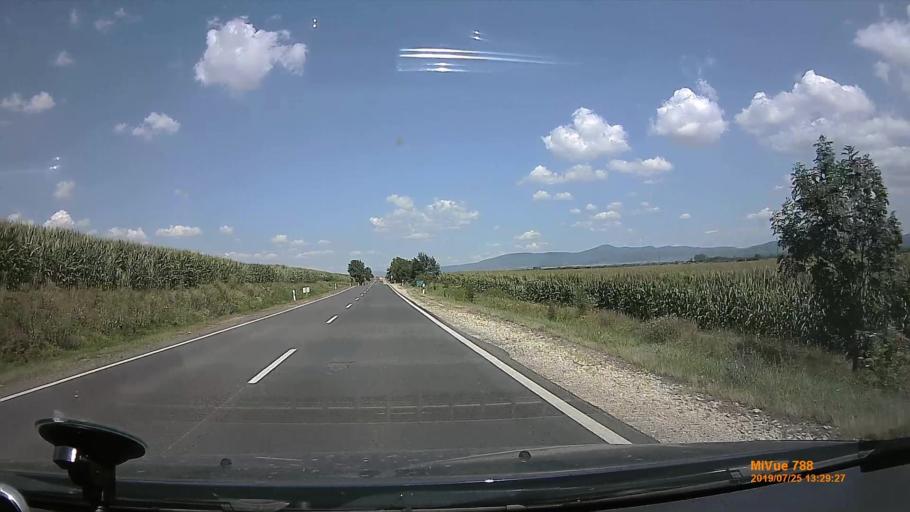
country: HU
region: Borsod-Abauj-Zemplen
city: Encs
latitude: 48.3432
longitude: 21.1165
